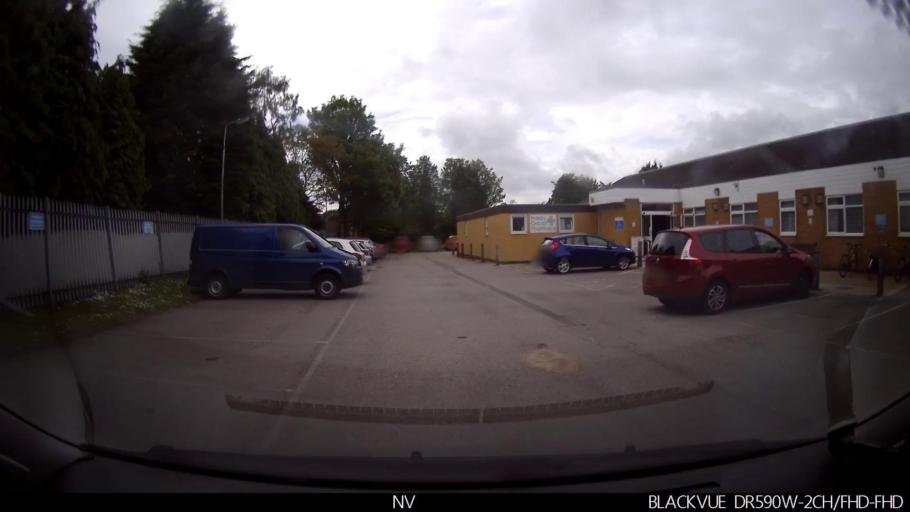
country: GB
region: England
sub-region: City of York
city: Wigginton
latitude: 54.0192
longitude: -1.0814
